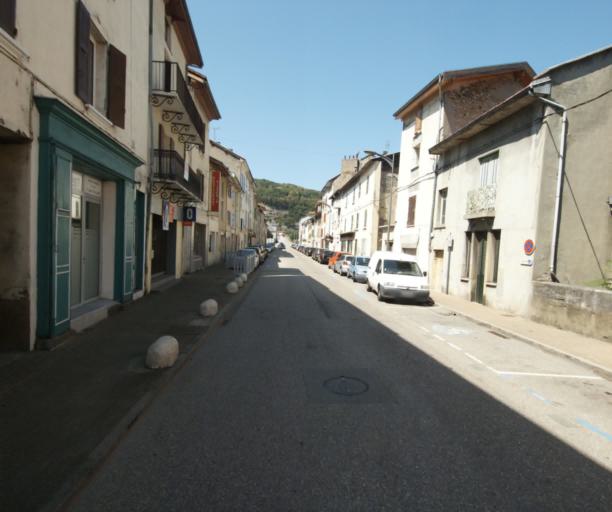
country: FR
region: Rhone-Alpes
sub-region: Departement de l'Isere
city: Vizille
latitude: 45.0756
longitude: 5.7712
